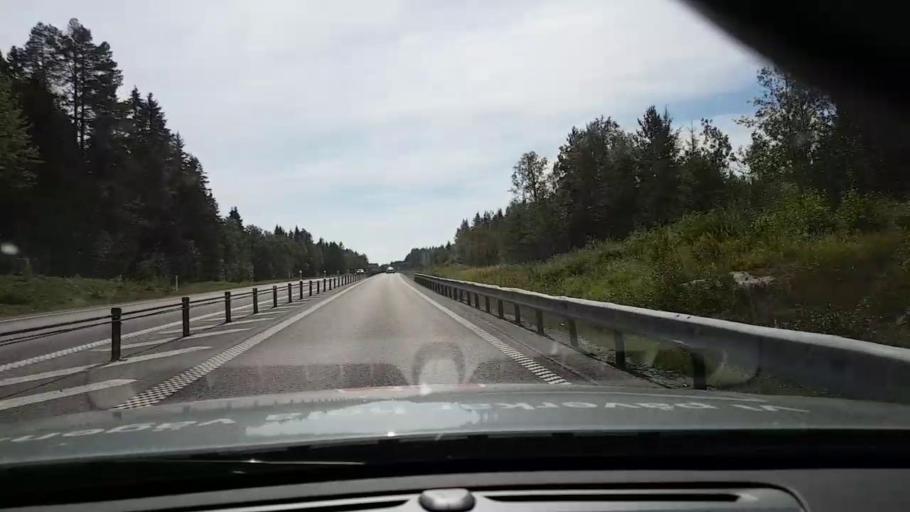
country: SE
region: Vaesternorrland
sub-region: OErnskoeldsviks Kommun
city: Husum
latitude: 63.4014
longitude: 19.2012
